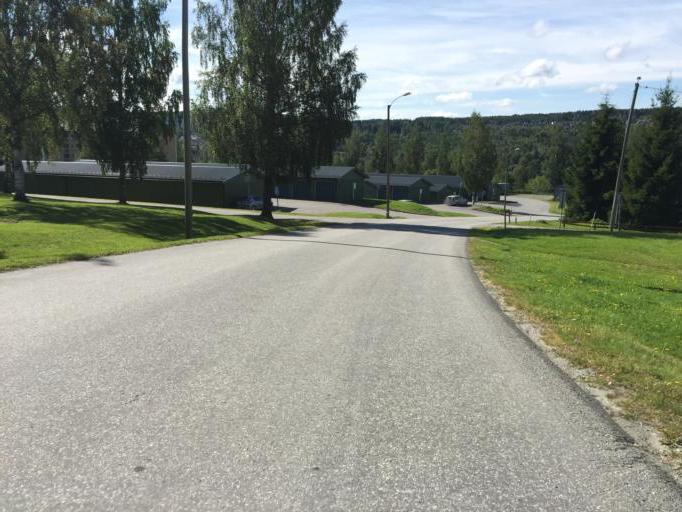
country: NO
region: Hedmark
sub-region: Kongsvinger
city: Kongsvinger
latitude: 60.1994
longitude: 11.9857
